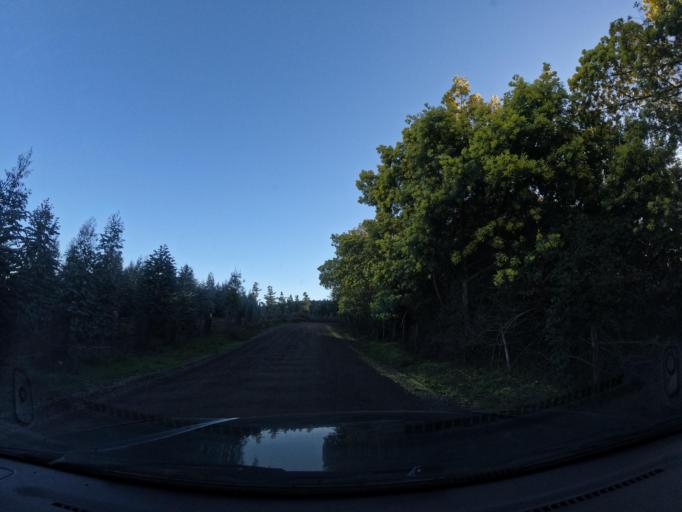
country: CL
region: Biobio
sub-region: Provincia de Concepcion
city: Chiguayante
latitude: -37.0165
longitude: -72.8511
